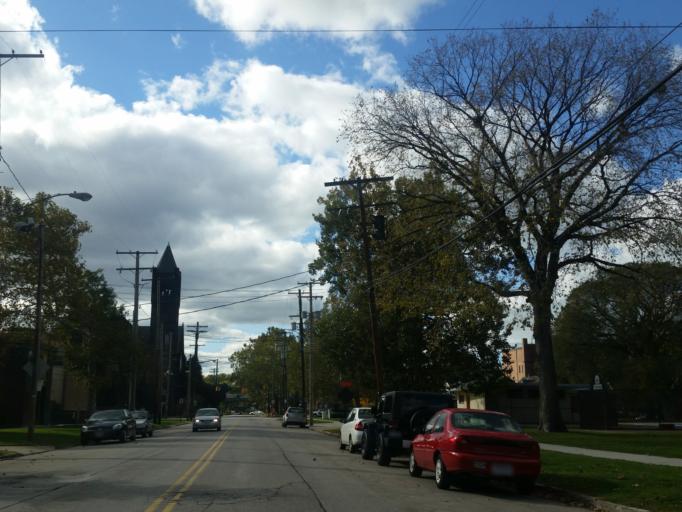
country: US
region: Ohio
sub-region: Cuyahoga County
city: Cleveland
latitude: 41.4775
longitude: -81.6895
